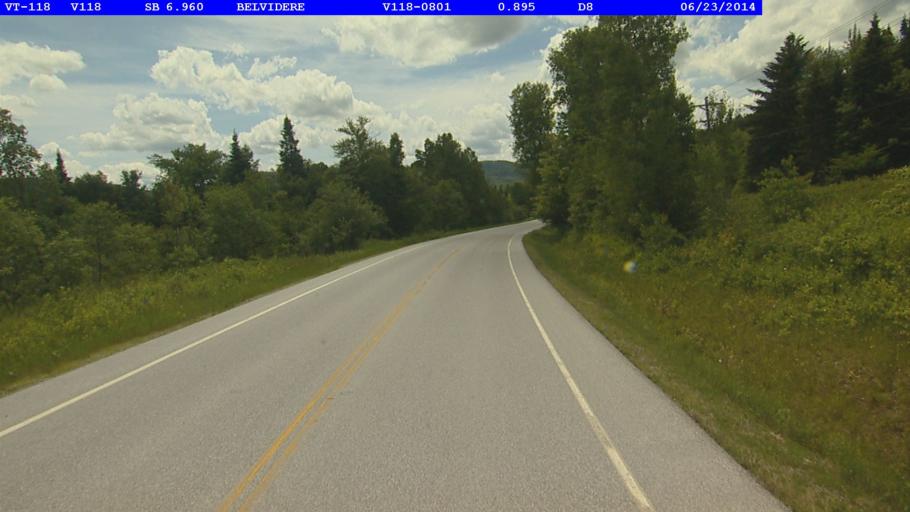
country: US
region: Vermont
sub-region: Lamoille County
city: Johnson
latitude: 44.7725
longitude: -72.6216
